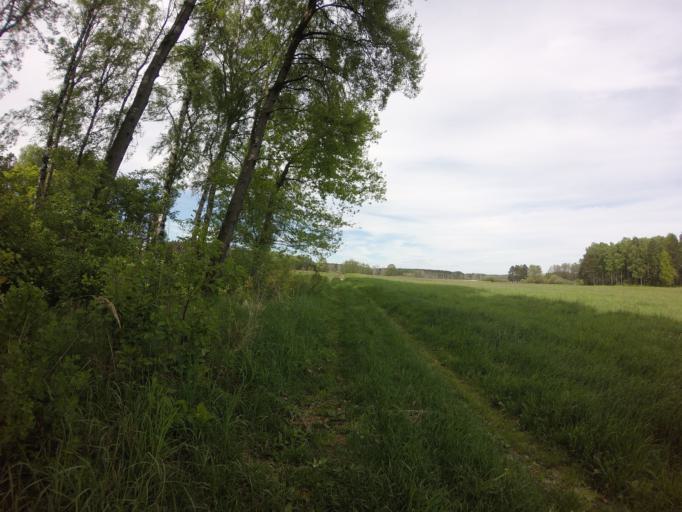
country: PL
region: West Pomeranian Voivodeship
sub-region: Powiat choszczenski
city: Drawno
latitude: 53.1572
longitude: 15.6647
